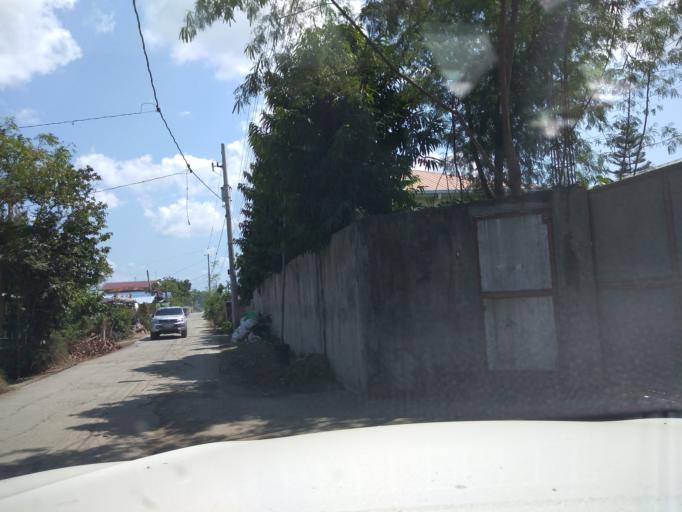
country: PH
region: Central Luzon
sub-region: Province of Pampanga
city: Bahay Pare
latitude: 15.0454
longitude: 120.8840
